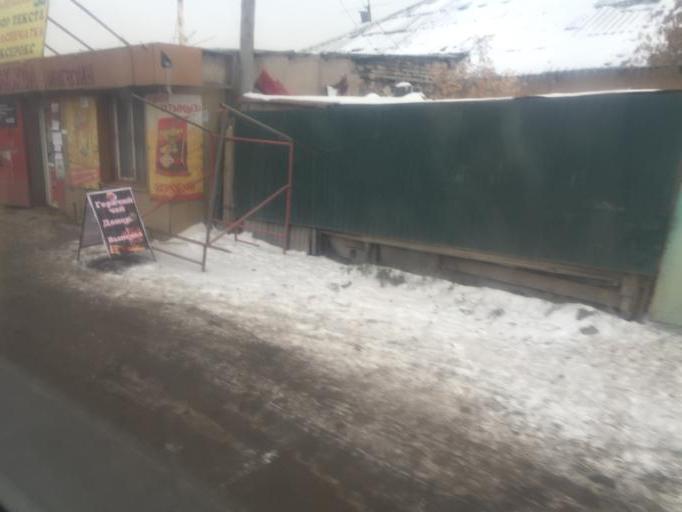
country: KZ
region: Astana Qalasy
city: Astana
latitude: 51.2064
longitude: 71.4124
